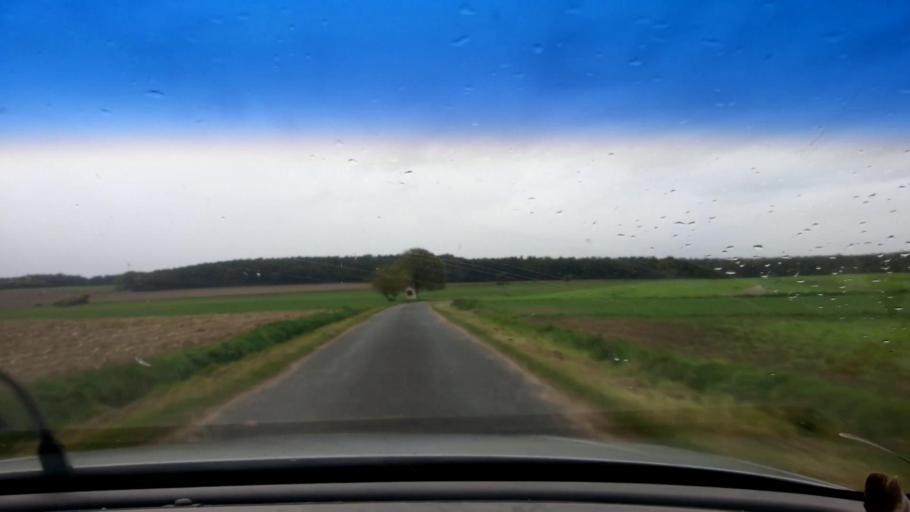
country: DE
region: Bavaria
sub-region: Upper Franconia
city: Burgwindheim
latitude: 49.8278
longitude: 10.6487
